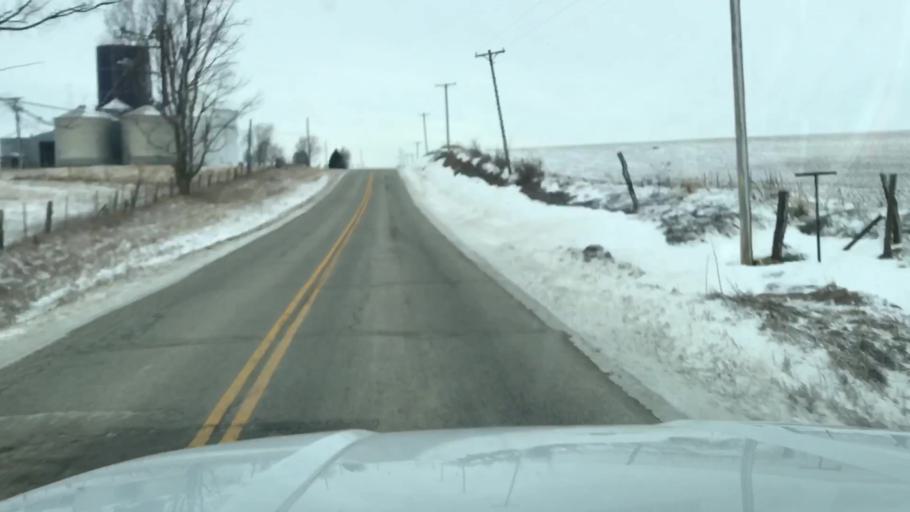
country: US
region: Missouri
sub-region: Andrew County
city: Savannah
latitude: 40.0250
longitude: -94.9512
